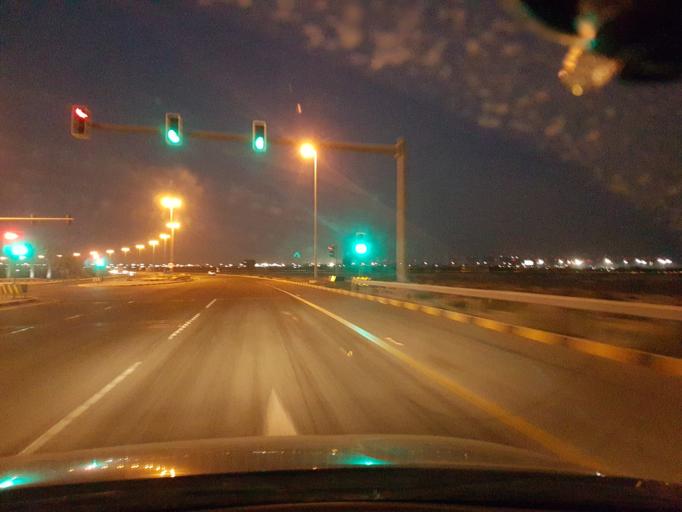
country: BH
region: Central Governorate
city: Dar Kulayb
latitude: 26.0272
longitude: 50.4962
